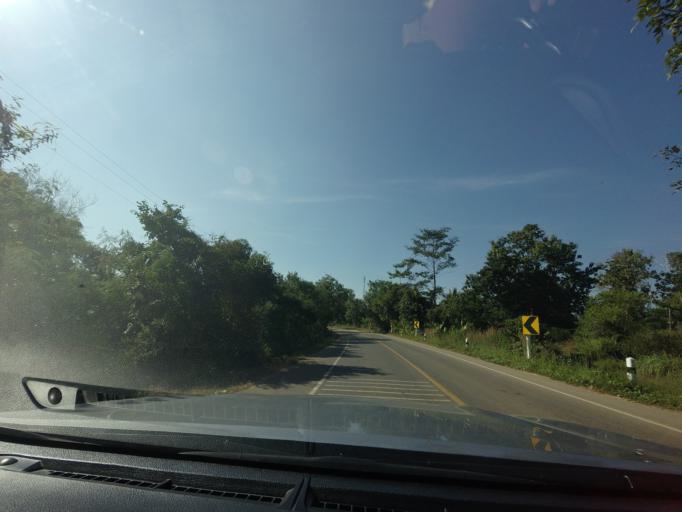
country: TH
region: Sukhothai
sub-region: Amphoe Si Satchanalai
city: Si Satchanalai
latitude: 17.6944
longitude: 99.7072
